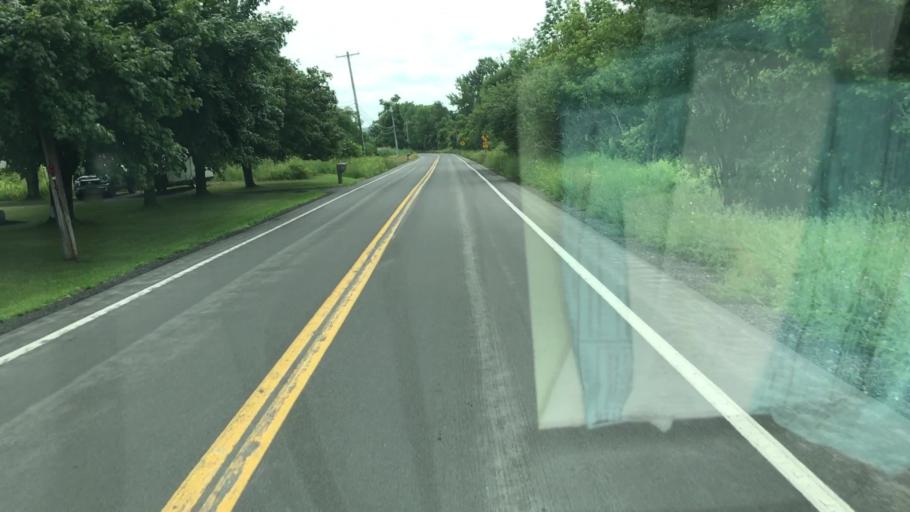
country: US
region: New York
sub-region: Onondaga County
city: Manlius
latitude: 42.9727
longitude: -75.9888
